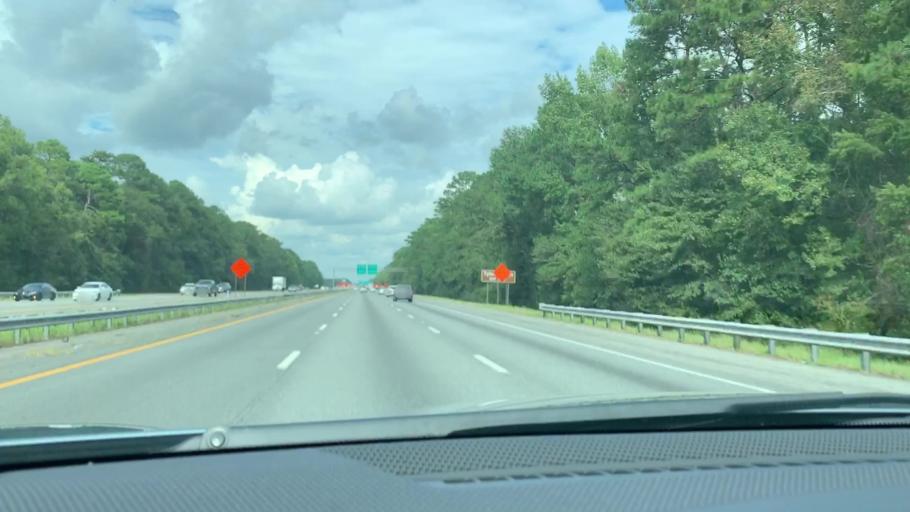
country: US
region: Georgia
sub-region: Chatham County
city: Pooler
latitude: 32.0616
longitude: -81.2522
